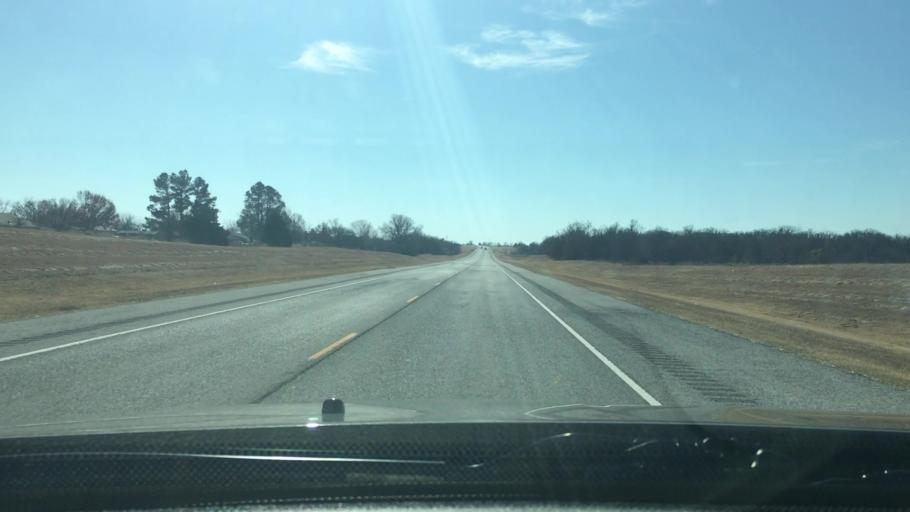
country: US
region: Oklahoma
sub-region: Stephens County
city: Meridian
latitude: 34.4120
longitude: -97.9741
